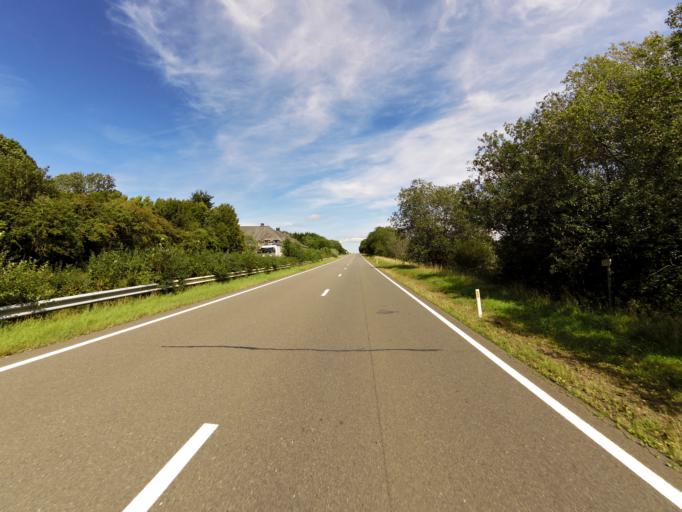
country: BE
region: Wallonia
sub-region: Province du Luxembourg
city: Tenneville
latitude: 50.0892
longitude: 5.4490
